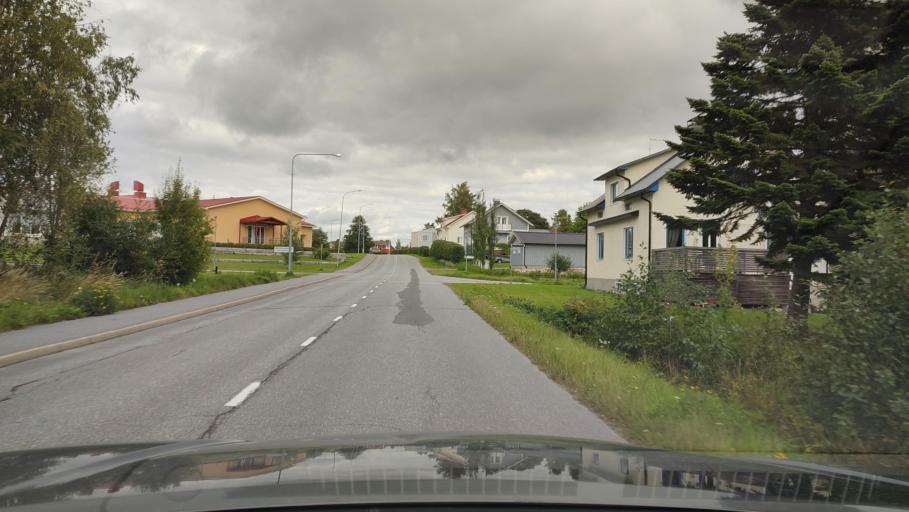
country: FI
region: Ostrobothnia
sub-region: Sydosterbotten
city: Kristinestad
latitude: 62.2672
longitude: 21.3693
